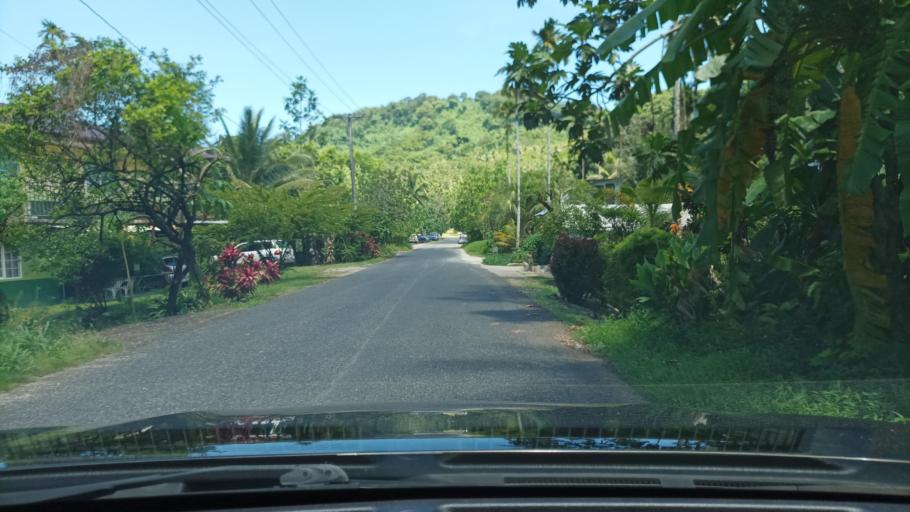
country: FM
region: Pohnpei
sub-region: Kolonia Municipality
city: Kolonia
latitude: 6.9612
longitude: 158.2652
